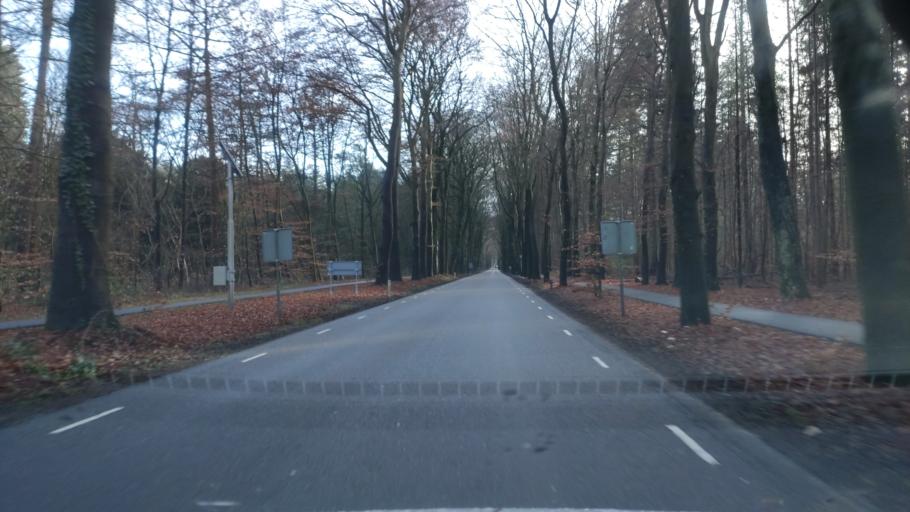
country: NL
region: Gelderland
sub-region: Gemeente Putten
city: Putten
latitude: 52.2504
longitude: 5.6288
